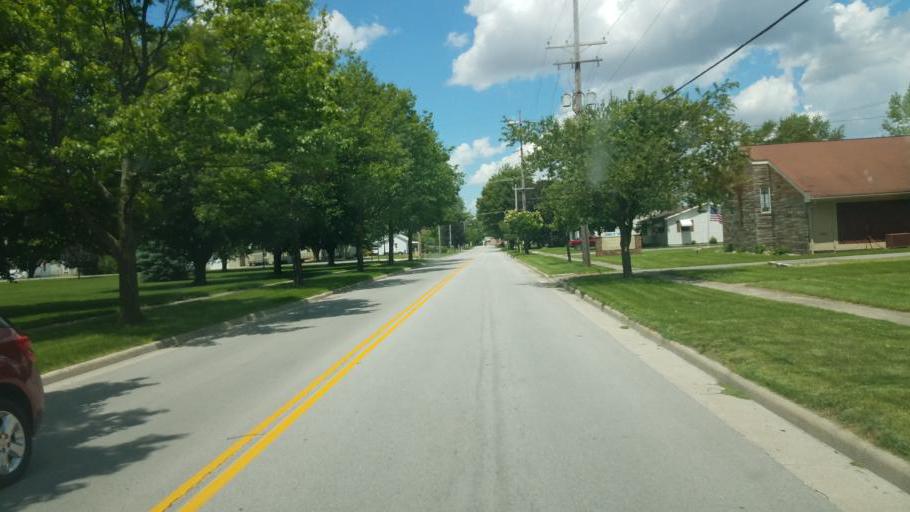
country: US
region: Ohio
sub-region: Wyandot County
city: Upper Sandusky
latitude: 40.8149
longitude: -83.2842
